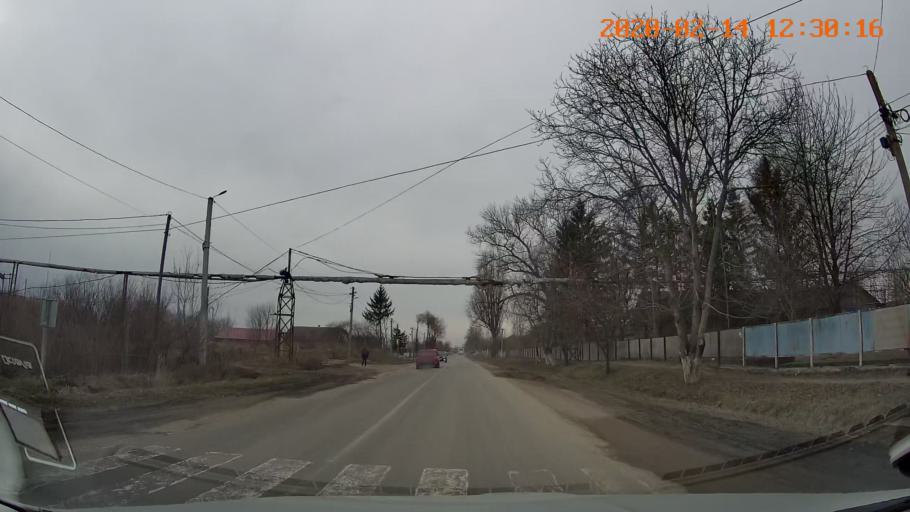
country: RO
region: Botosani
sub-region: Comuna Darabani
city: Bajura
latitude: 48.2528
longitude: 26.5701
